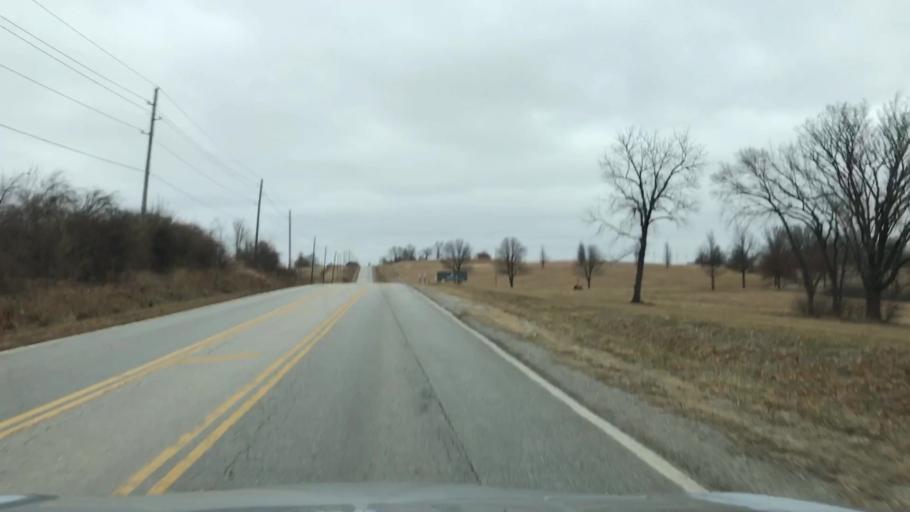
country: US
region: Missouri
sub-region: Clay County
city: Liberty
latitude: 39.2671
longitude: -94.4166
